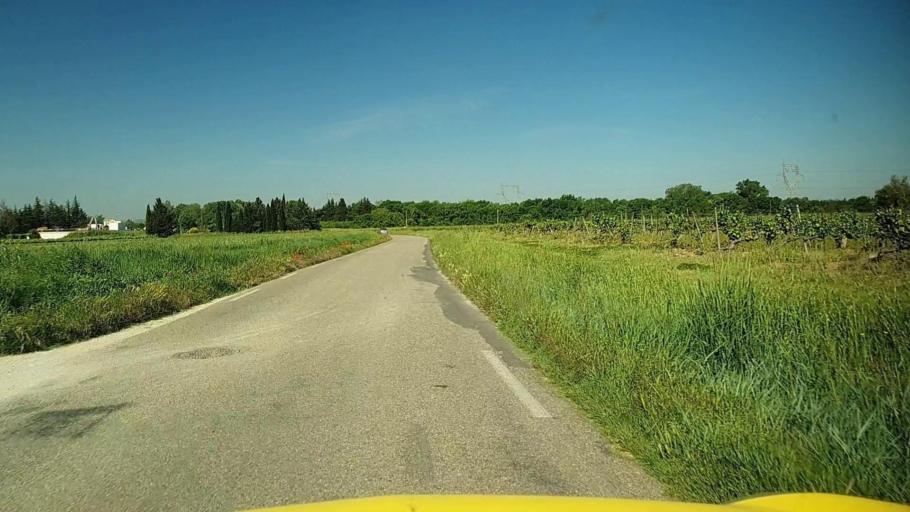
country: FR
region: Languedoc-Roussillon
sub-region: Departement du Gard
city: Saint-Chaptes
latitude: 43.9423
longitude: 4.3189
